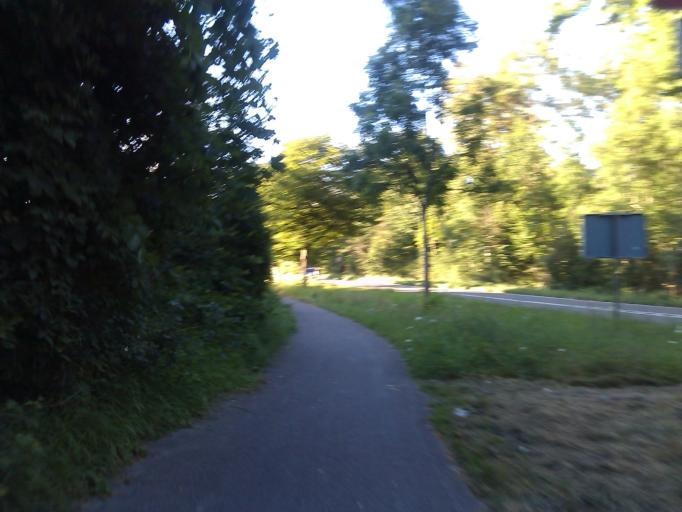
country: DE
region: Rheinland-Pfalz
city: Altrip
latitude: 49.4116
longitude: 8.4879
